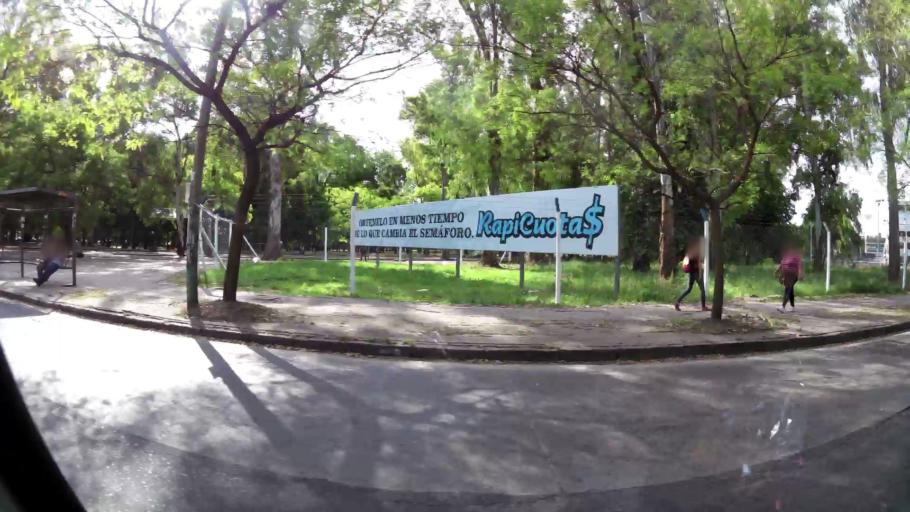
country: AR
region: Buenos Aires
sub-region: Partido de La Plata
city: La Plata
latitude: -34.9130
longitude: -57.9330
